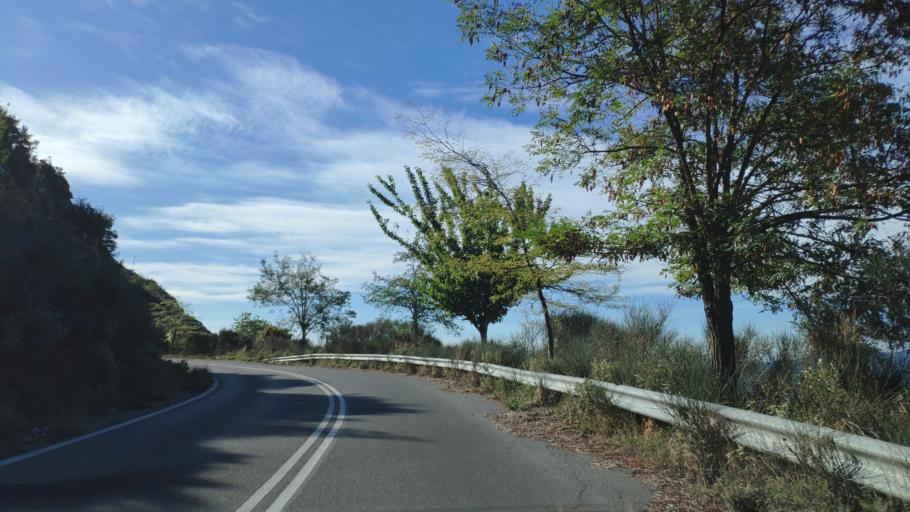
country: GR
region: Peloponnese
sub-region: Nomos Arkadias
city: Dimitsana
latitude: 37.5541
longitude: 22.0636
